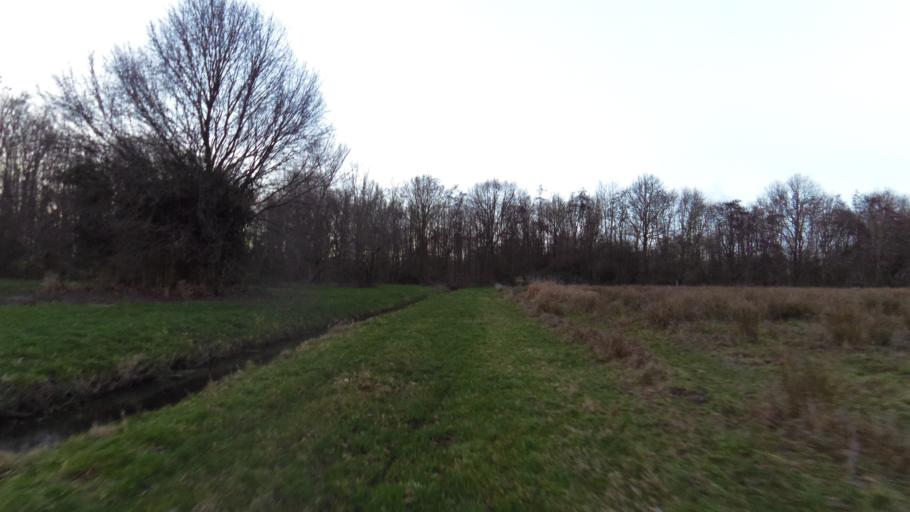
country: NL
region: South Holland
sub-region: Gemeente Noordwijkerhout
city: Noordwijkerhout
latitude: 52.2749
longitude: 4.4900
